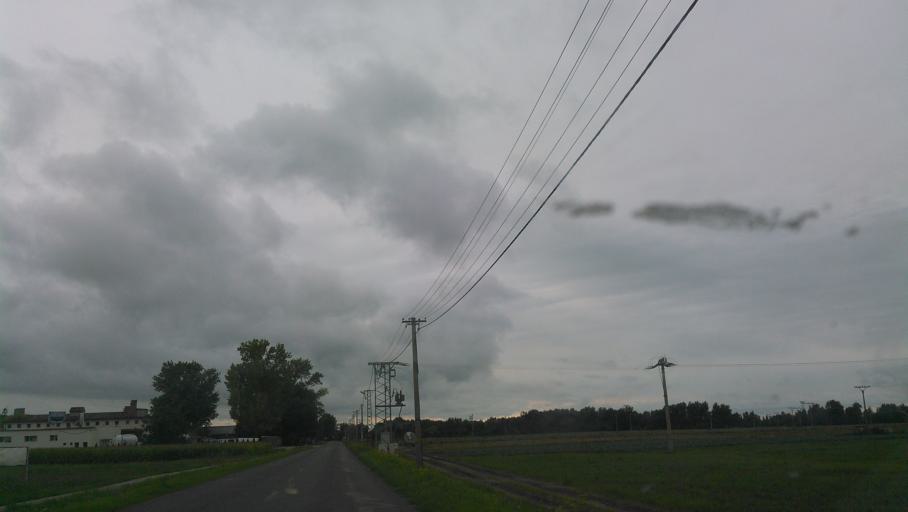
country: SK
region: Trnavsky
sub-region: Okres Dunajska Streda
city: Velky Meder
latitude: 47.8942
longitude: 17.8000
